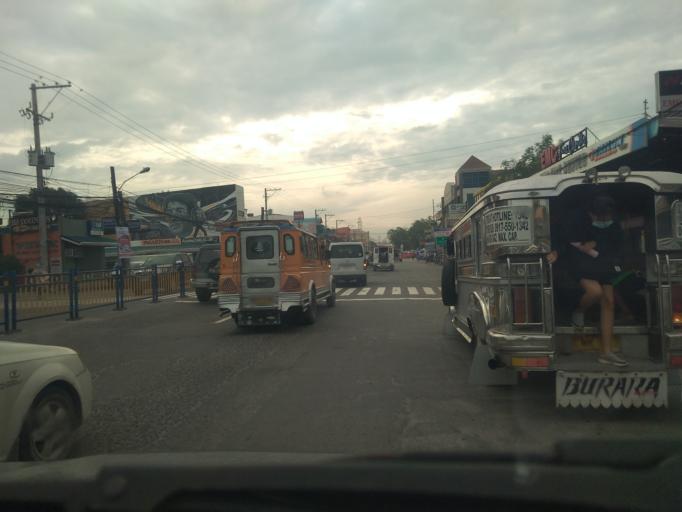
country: PH
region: Central Luzon
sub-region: Province of Pampanga
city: San Fernando
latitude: 15.0384
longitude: 120.6814
